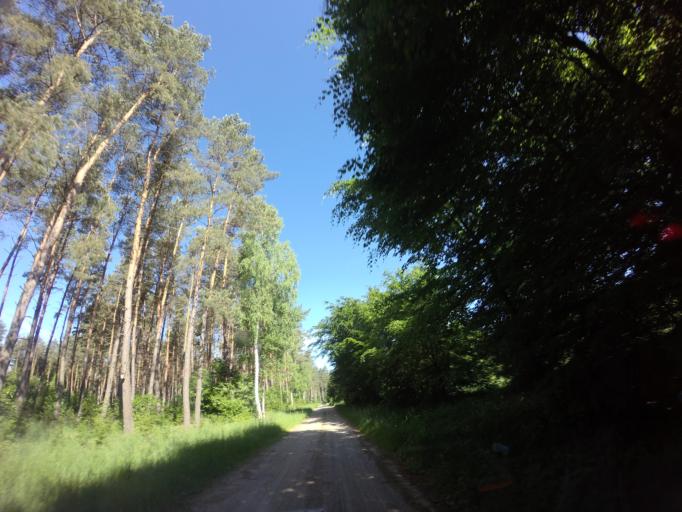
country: PL
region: West Pomeranian Voivodeship
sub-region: Powiat choszczenski
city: Drawno
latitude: 53.2253
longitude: 15.6771
